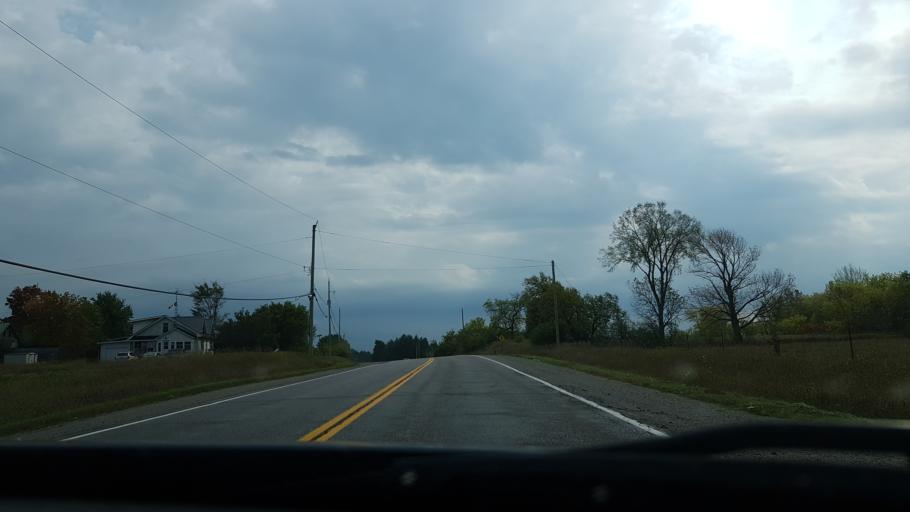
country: CA
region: Ontario
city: Omemee
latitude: 44.5161
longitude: -78.7436
